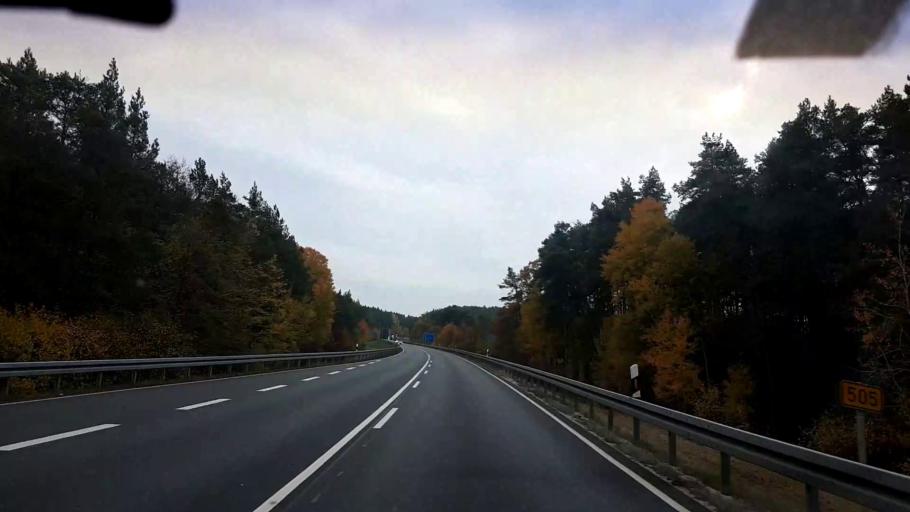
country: DE
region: Bavaria
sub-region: Upper Franconia
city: Pommersfelden
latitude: 49.7411
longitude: 10.8272
